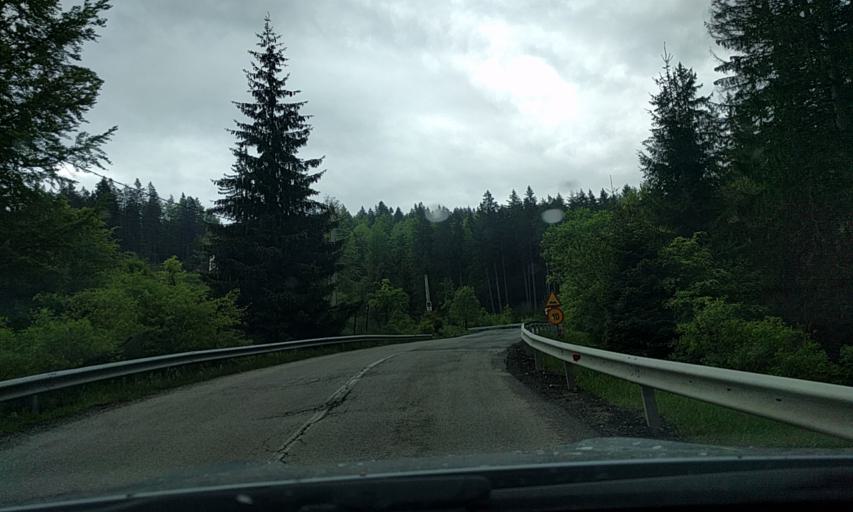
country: RO
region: Prahova
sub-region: Oras Sinaia
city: Sinaia
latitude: 45.3068
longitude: 25.5212
